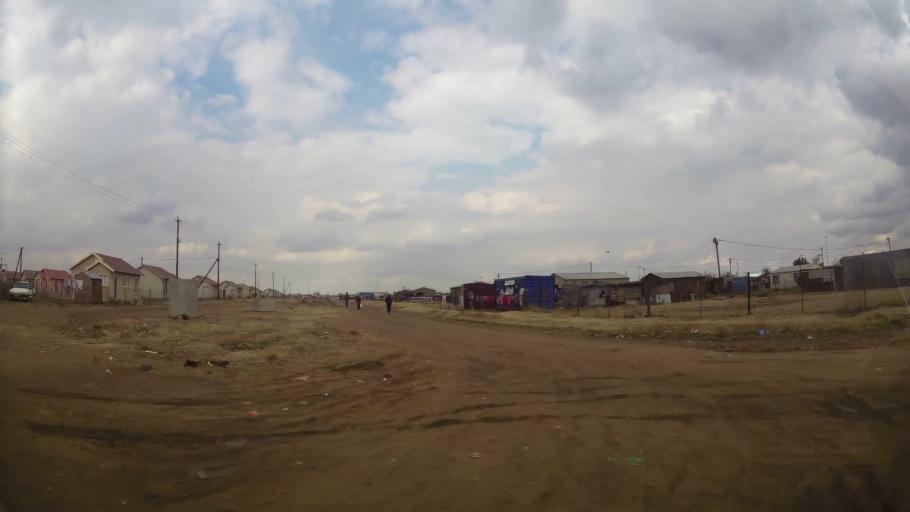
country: ZA
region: Orange Free State
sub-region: Fezile Dabi District Municipality
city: Sasolburg
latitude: -26.8591
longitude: 27.8670
